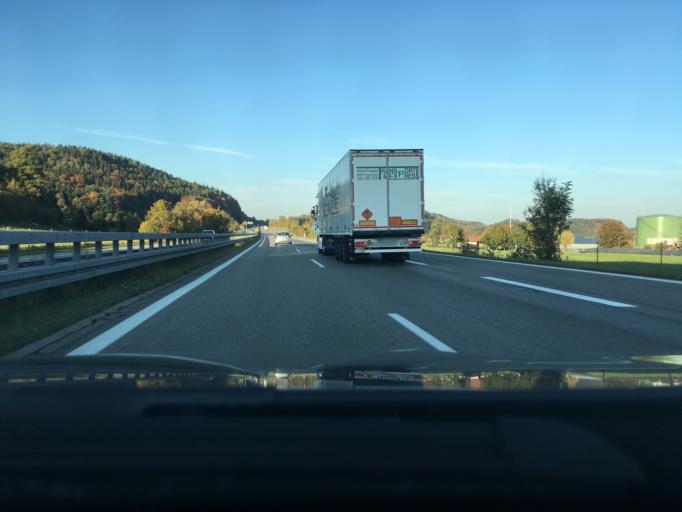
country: DE
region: Baden-Wuerttemberg
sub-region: Tuebingen Region
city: Aichstetten
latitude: 47.8808
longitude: 10.0378
